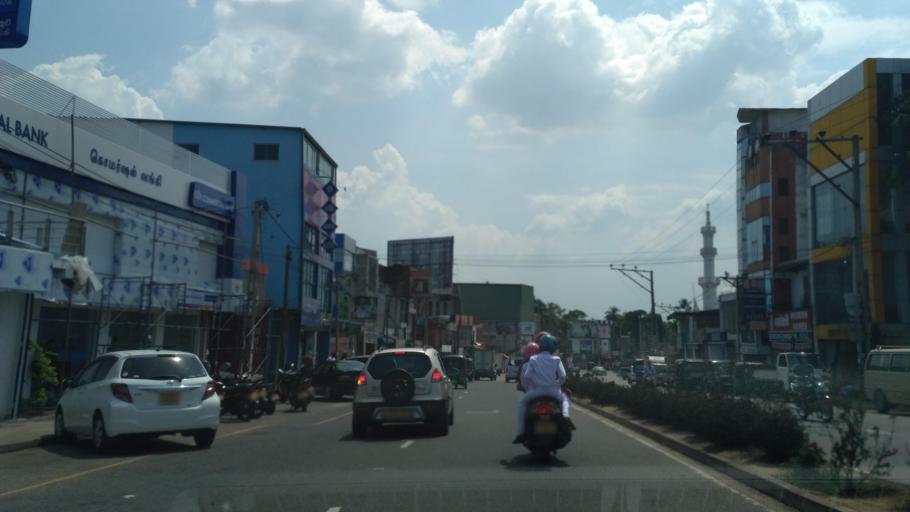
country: LK
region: North Western
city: Kurunegala
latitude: 7.4299
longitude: 80.2145
